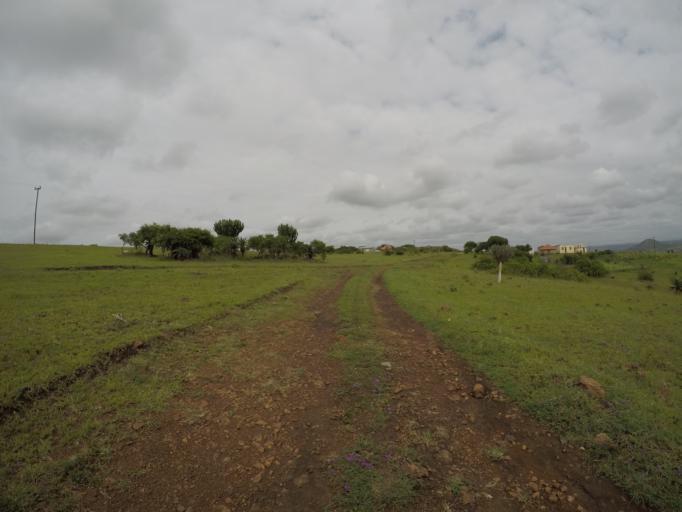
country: ZA
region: KwaZulu-Natal
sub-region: uThungulu District Municipality
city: Empangeni
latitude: -28.6160
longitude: 31.8972
